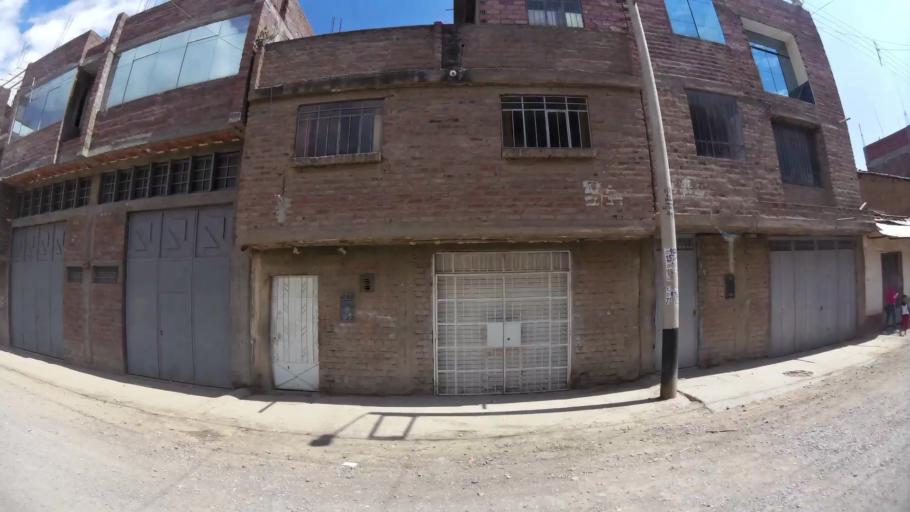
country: PE
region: Junin
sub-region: Provincia de Huancayo
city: Huancayo
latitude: -12.0682
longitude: -75.1998
